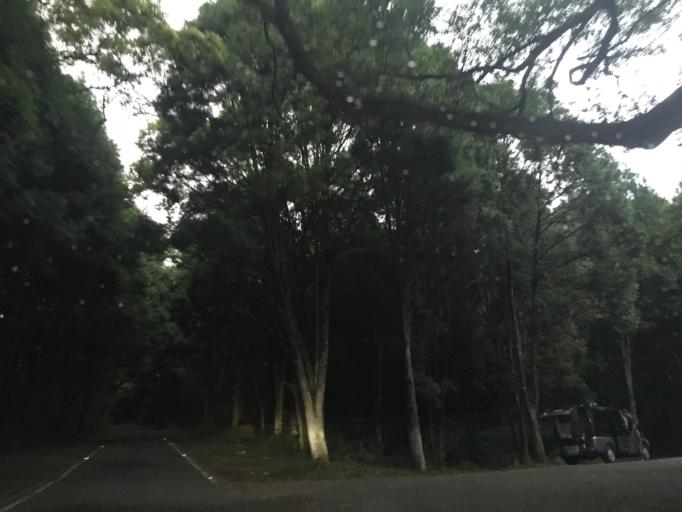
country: TW
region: Taiwan
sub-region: Nantou
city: Puli
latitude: 23.9040
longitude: 120.9060
